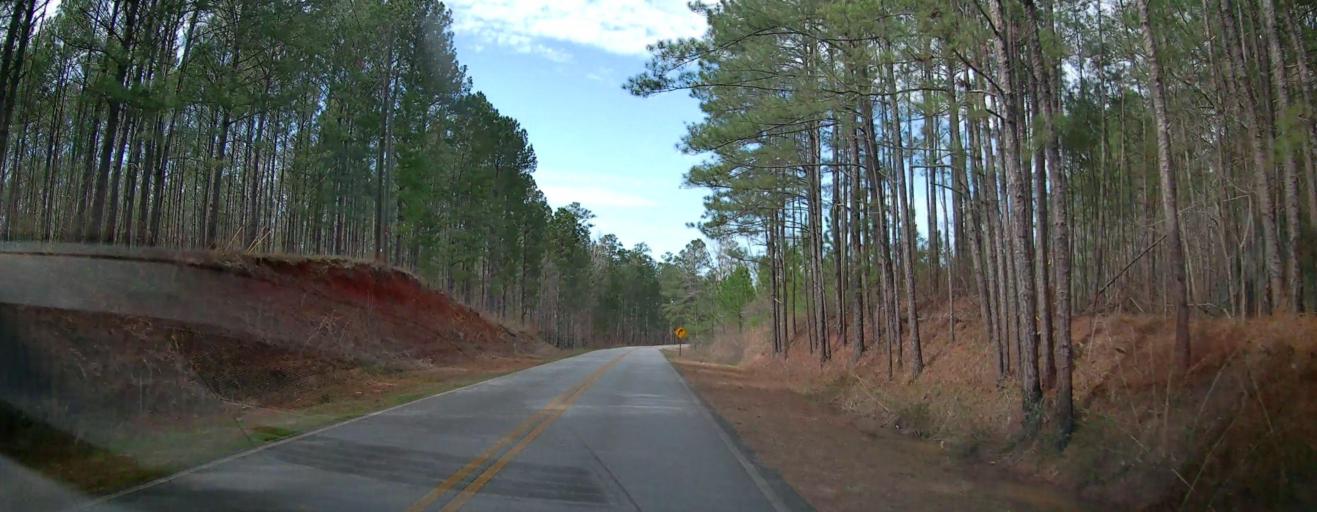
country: US
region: Georgia
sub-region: Jones County
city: Gray
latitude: 33.0414
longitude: -83.7133
